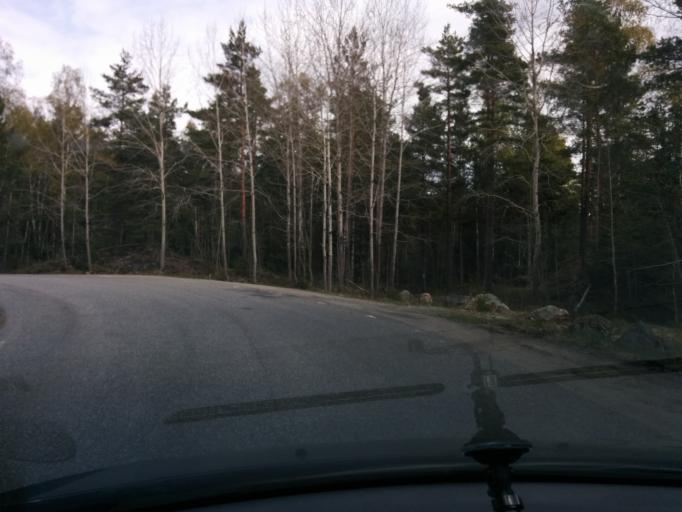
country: SE
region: Stockholm
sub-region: Botkyrka Kommun
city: Tullinge
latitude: 59.2311
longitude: 17.8926
